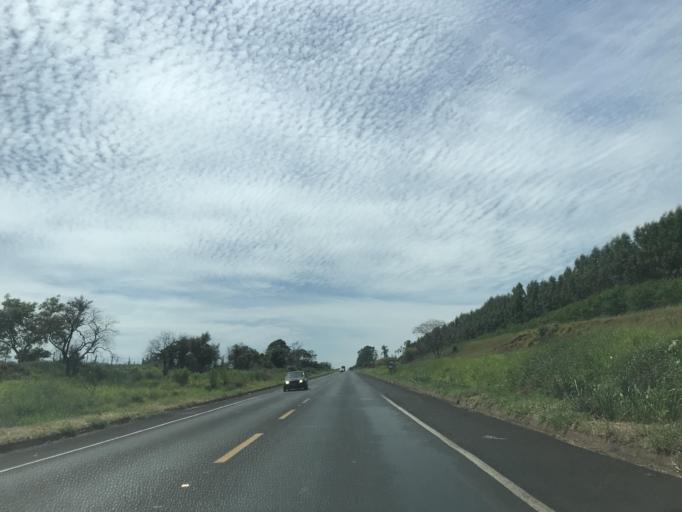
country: BR
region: Parana
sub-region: Paranavai
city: Paranavai
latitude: -22.9996
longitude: -52.5673
